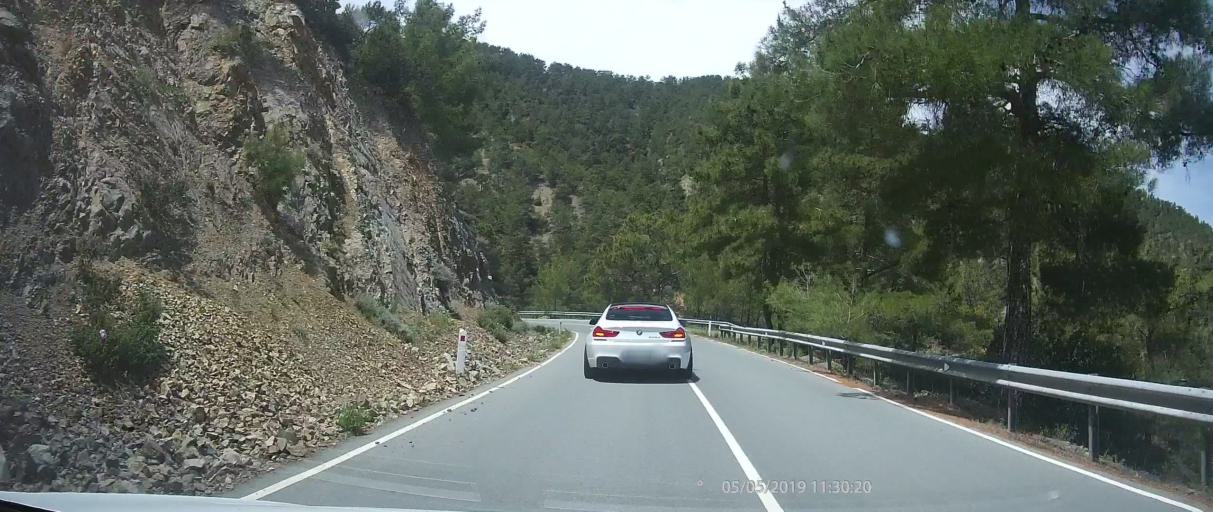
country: CY
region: Limassol
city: Pachna
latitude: 34.9454
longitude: 32.6486
